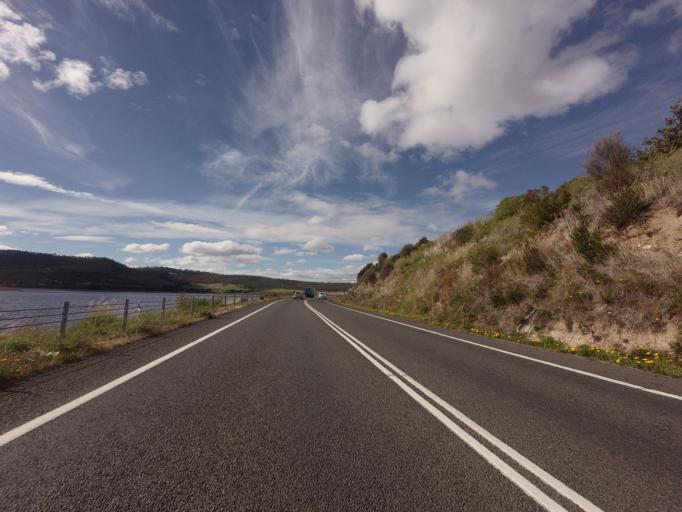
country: AU
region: Tasmania
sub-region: Brighton
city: Bridgewater
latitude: -42.7420
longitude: 147.1940
